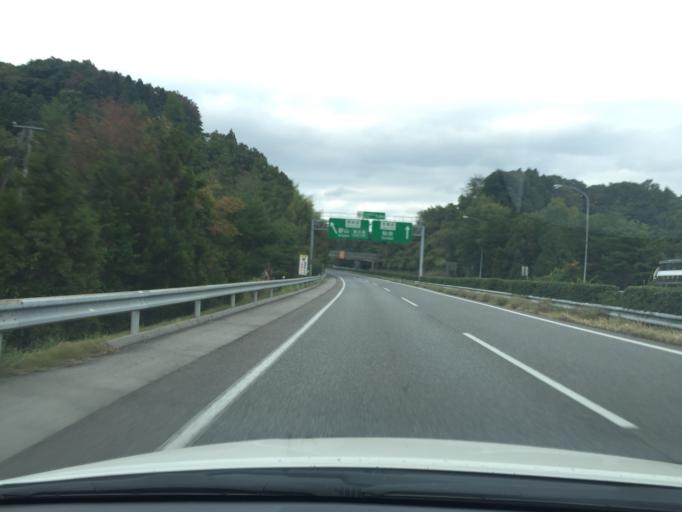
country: JP
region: Fukushima
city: Iwaki
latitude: 37.0248
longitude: 140.8140
